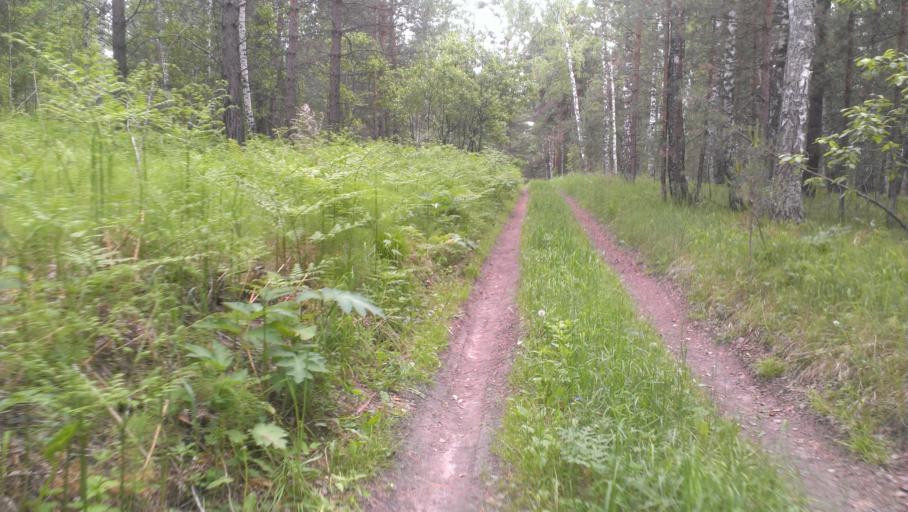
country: RU
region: Altai Krai
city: Sannikovo
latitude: 53.3437
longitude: 84.0443
